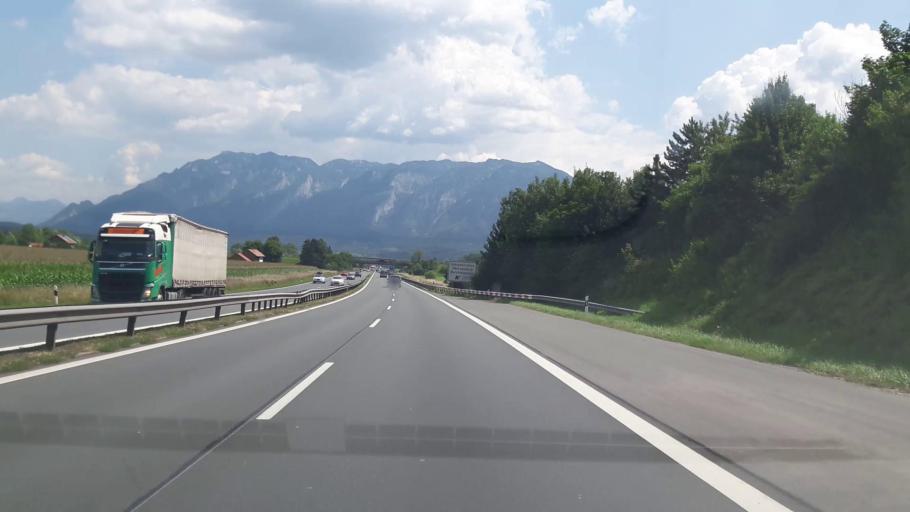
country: DE
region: Bavaria
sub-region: Upper Bavaria
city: Anger
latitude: 47.7820
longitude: 12.8760
